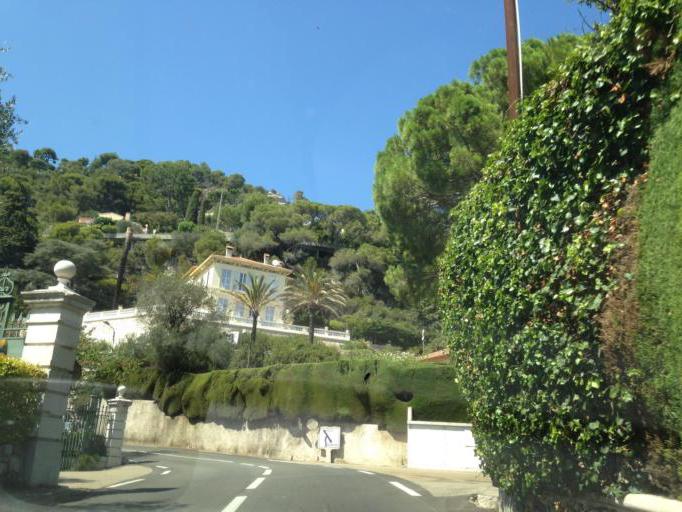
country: FR
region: Provence-Alpes-Cote d'Azur
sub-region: Departement des Alpes-Maritimes
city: Villefranche-sur-Mer
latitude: 43.7094
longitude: 7.3190
